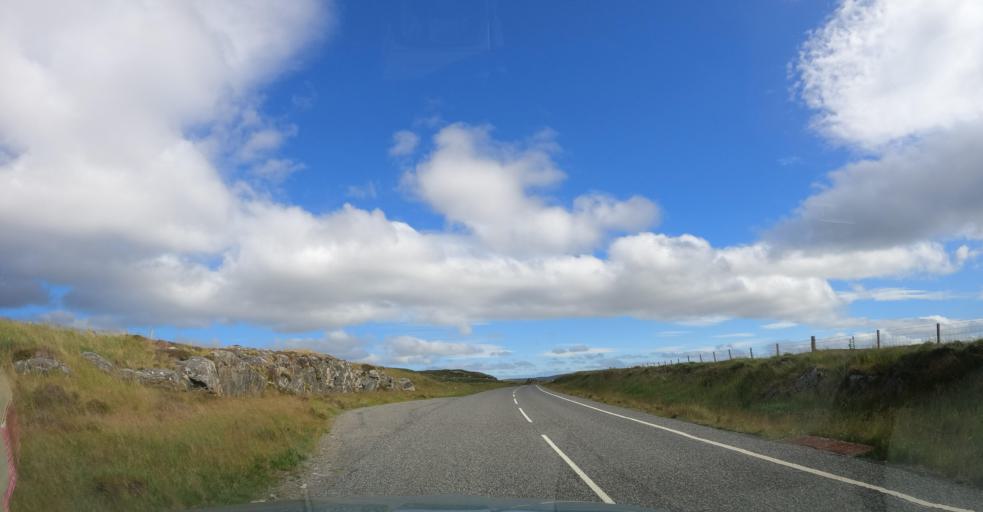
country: GB
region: Scotland
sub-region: Eilean Siar
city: Harris
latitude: 58.1956
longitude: -6.7183
